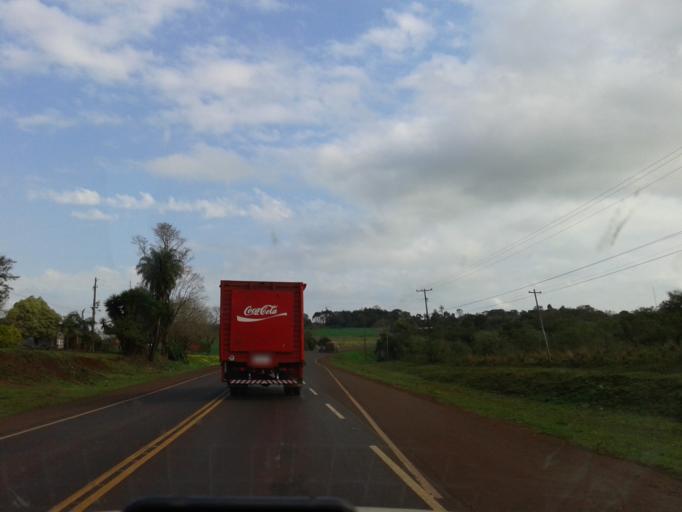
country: PY
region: Itapua
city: Edelira
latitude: -26.7172
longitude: -55.3311
